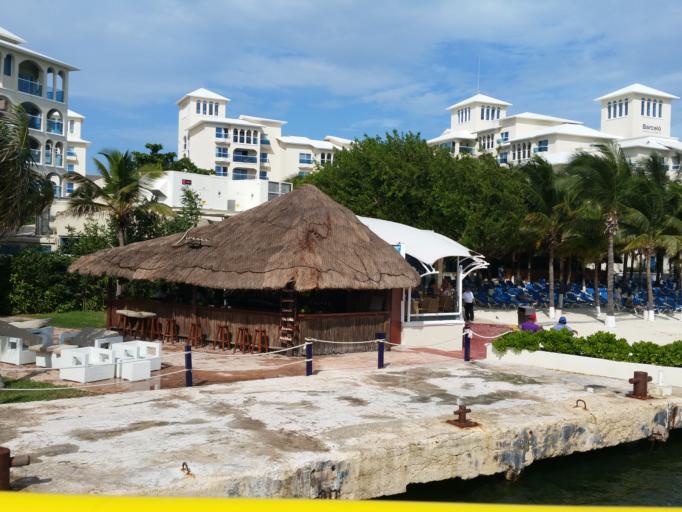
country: MX
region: Quintana Roo
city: Cancun
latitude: 21.1448
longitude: -86.7879
